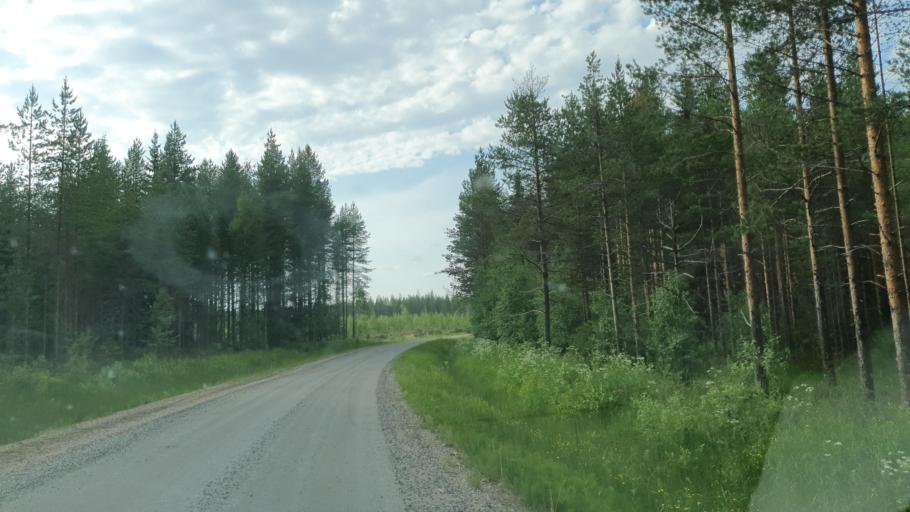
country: FI
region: Kainuu
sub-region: Kehys-Kainuu
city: Kuhmo
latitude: 64.0644
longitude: 29.7501
